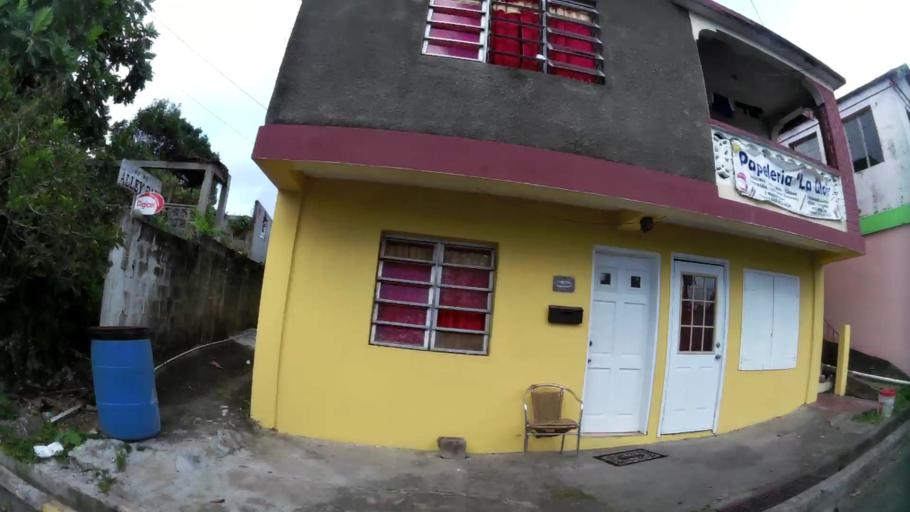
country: KN
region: Saint Mary Cayon
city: Cayon
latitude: 17.3507
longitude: -62.7324
